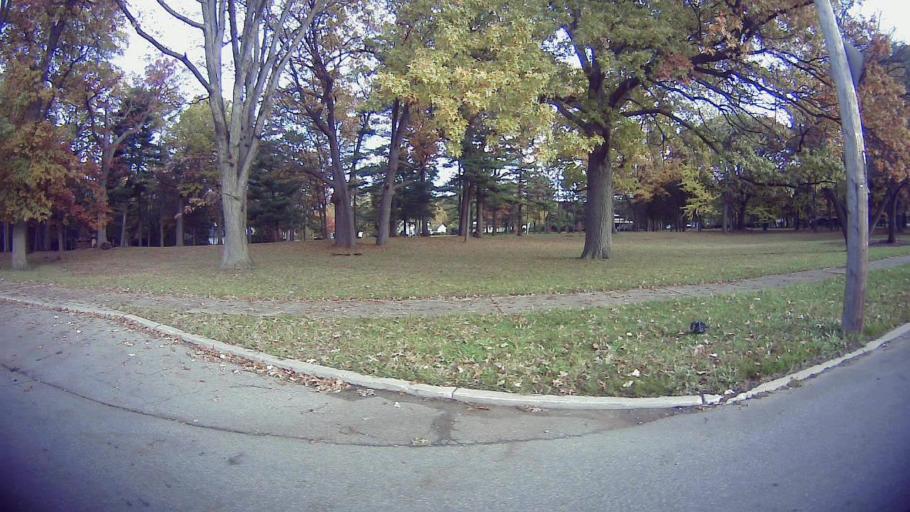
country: US
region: Michigan
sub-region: Oakland County
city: Ferndale
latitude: 42.4320
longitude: -83.1264
